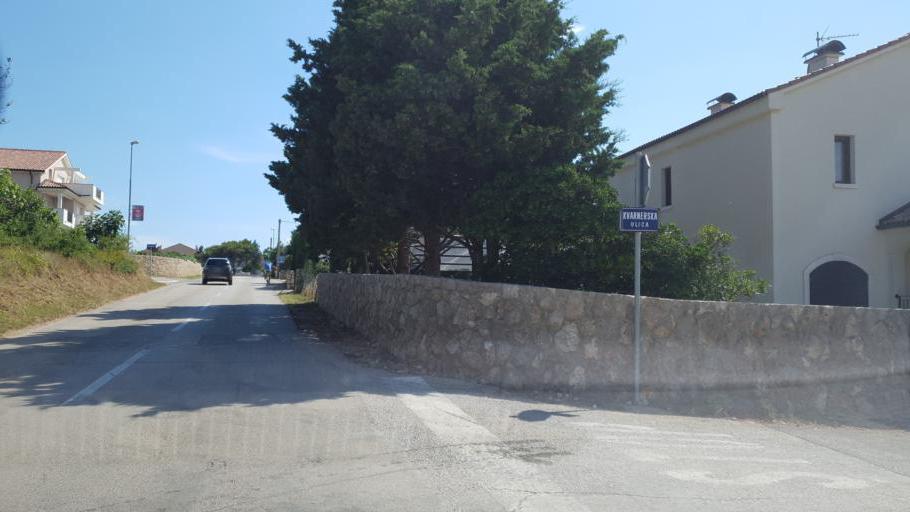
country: HR
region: Primorsko-Goranska
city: Punat
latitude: 45.0146
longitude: 14.6306
